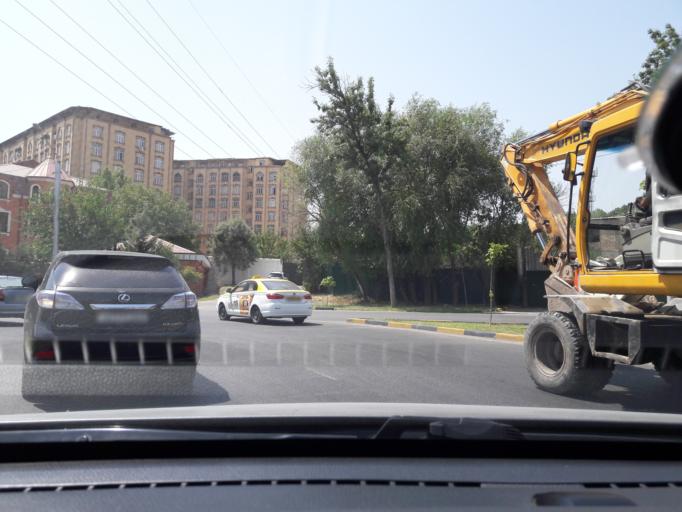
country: TJ
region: Dushanbe
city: Dushanbe
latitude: 38.5920
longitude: 68.7429
